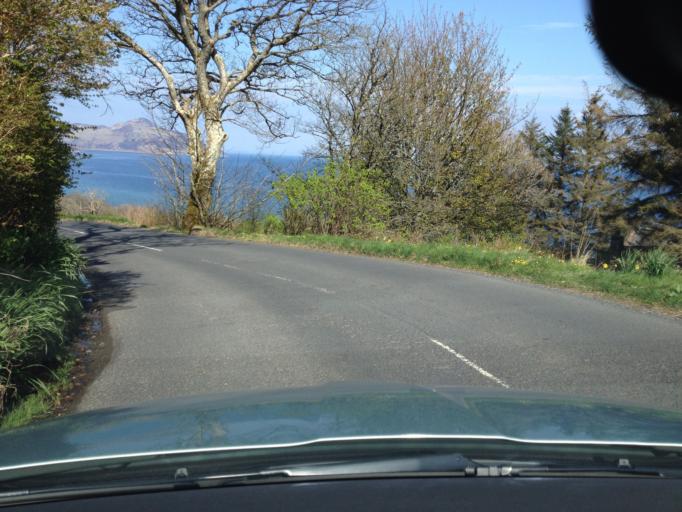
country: GB
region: Scotland
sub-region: North Ayrshire
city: Lamlash
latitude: 55.4657
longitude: -5.0856
